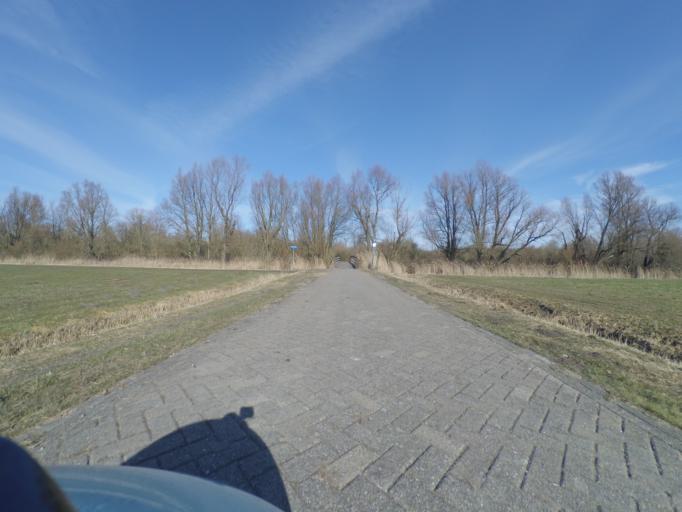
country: NL
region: Flevoland
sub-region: Gemeente Almere
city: Almere Stad
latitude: 52.4043
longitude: 5.2258
